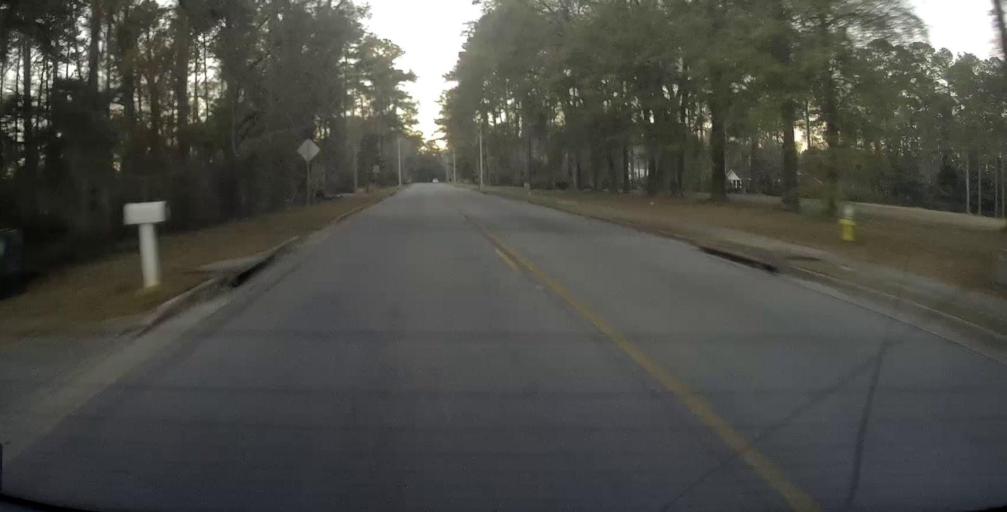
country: US
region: Georgia
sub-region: Dougherty County
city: Albany
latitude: 31.5309
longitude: -84.1368
